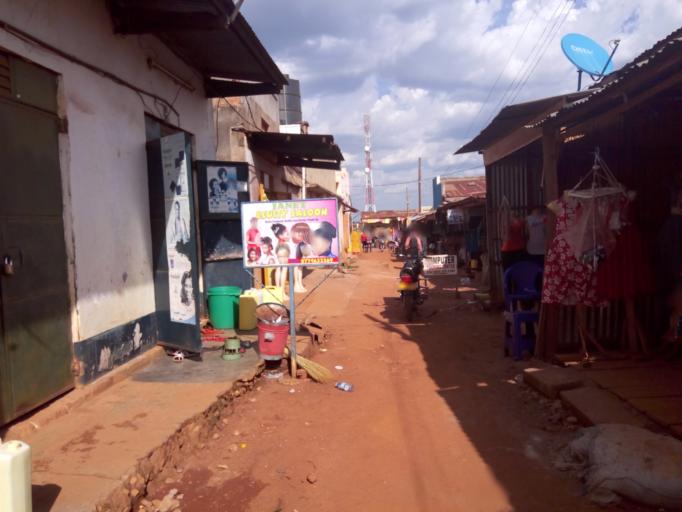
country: UG
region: Western Region
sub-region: Masindi District
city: Masindi
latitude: 1.6826
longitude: 31.7207
